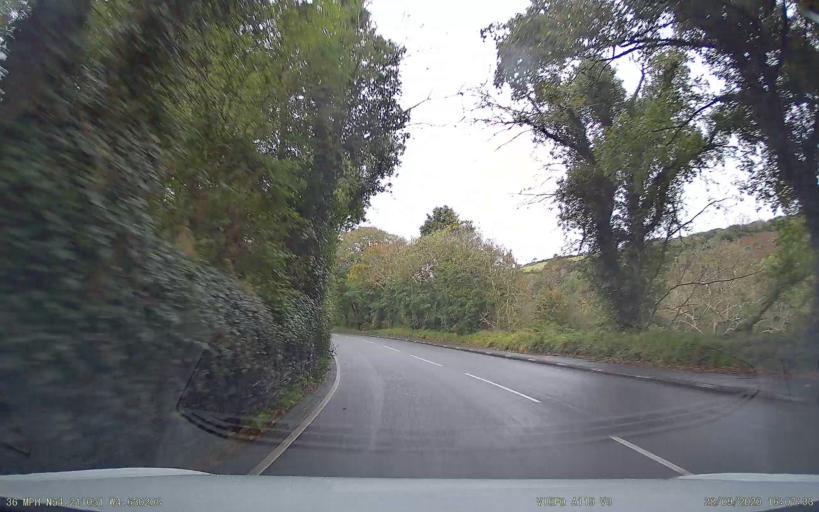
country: IM
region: Castletown
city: Castletown
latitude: 54.2111
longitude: -4.6302
